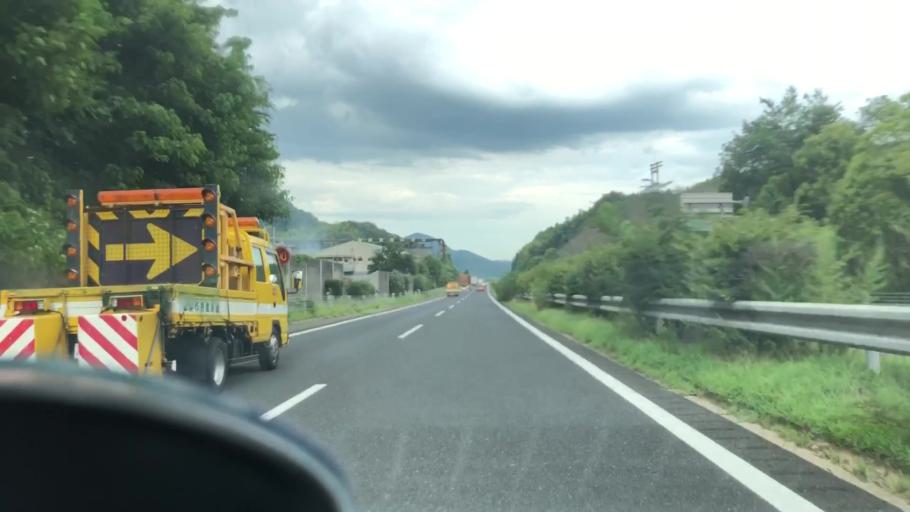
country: JP
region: Hyogo
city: Yamazakicho-nakabirose
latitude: 34.9737
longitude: 134.6538
